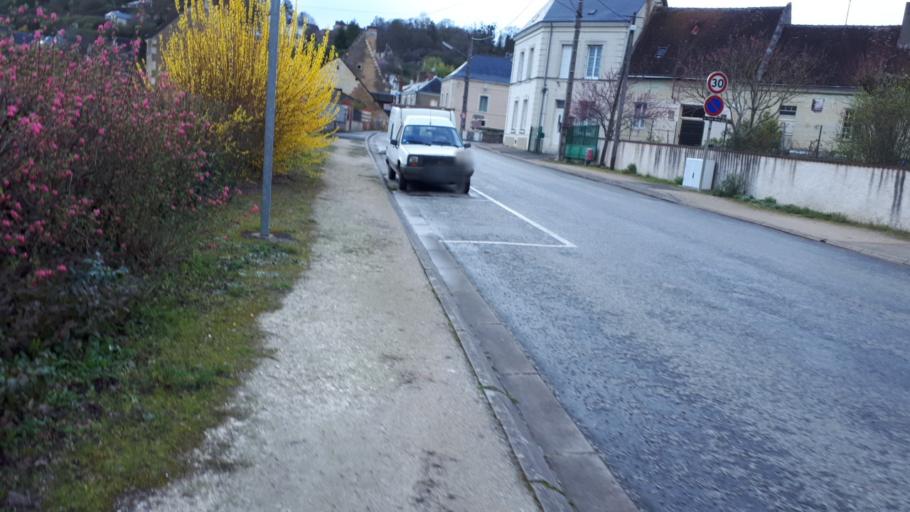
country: FR
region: Centre
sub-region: Departement du Loir-et-Cher
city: Montoire-sur-le-Loir
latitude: 47.7766
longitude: 0.7998
